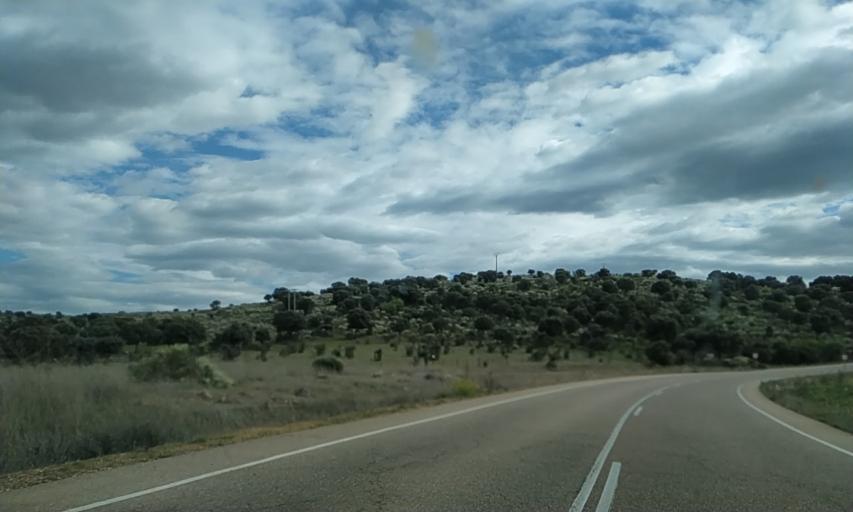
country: ES
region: Castille and Leon
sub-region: Provincia de Salamanca
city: Pastores
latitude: 40.5027
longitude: -6.5758
